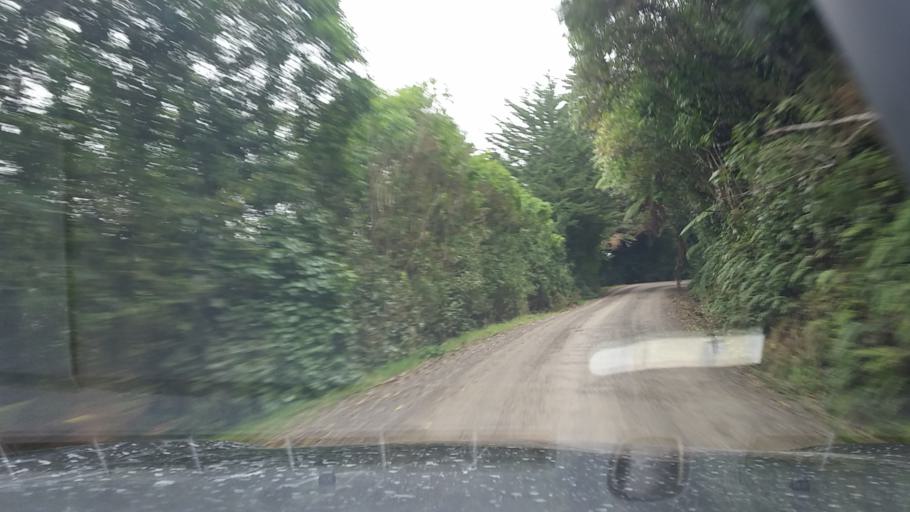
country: NZ
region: Marlborough
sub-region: Marlborough District
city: Picton
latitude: -41.1784
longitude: 173.9939
